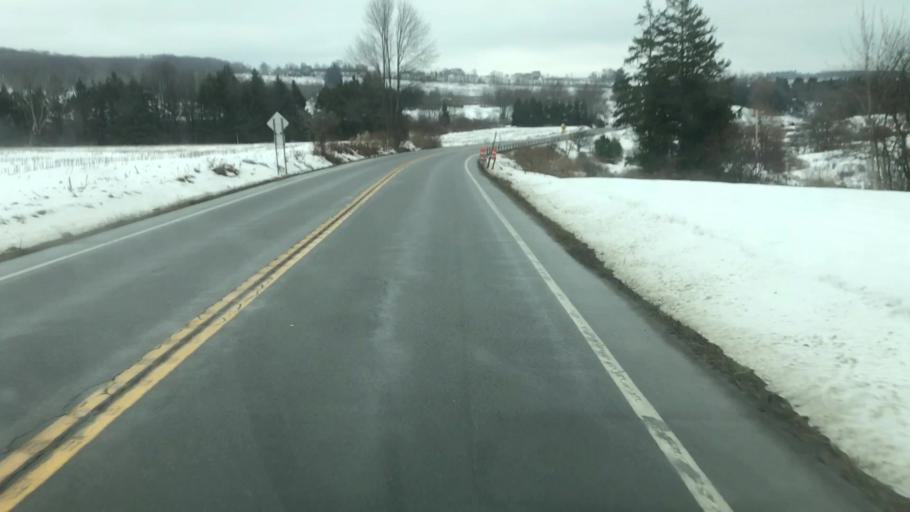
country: US
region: New York
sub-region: Cortland County
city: Cortland West
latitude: 42.6428
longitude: -76.2409
